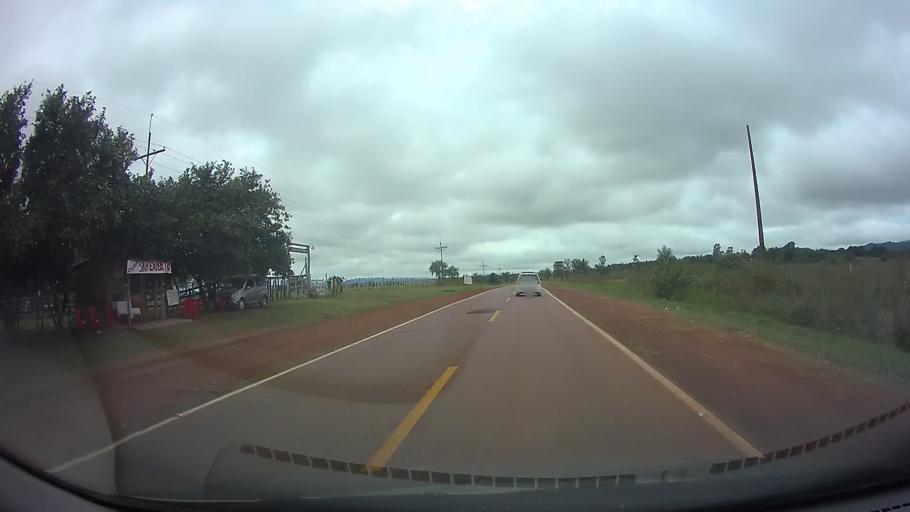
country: PY
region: Paraguari
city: Carapegua
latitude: -25.8122
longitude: -57.1789
